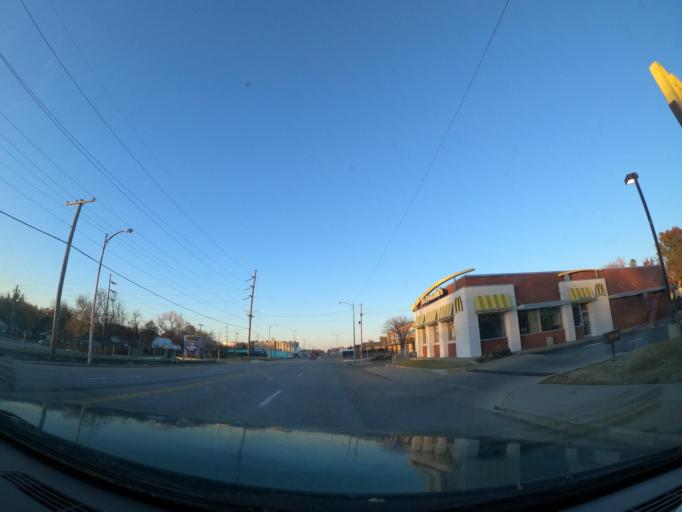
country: US
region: Oklahoma
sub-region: Tulsa County
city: Tulsa
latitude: 36.1437
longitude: -95.9403
